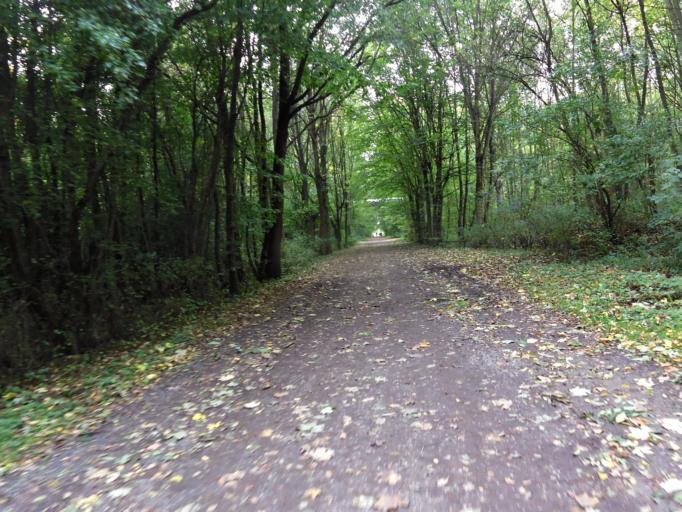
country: DE
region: Saxony
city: Markkleeberg
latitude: 51.2954
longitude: 12.3594
